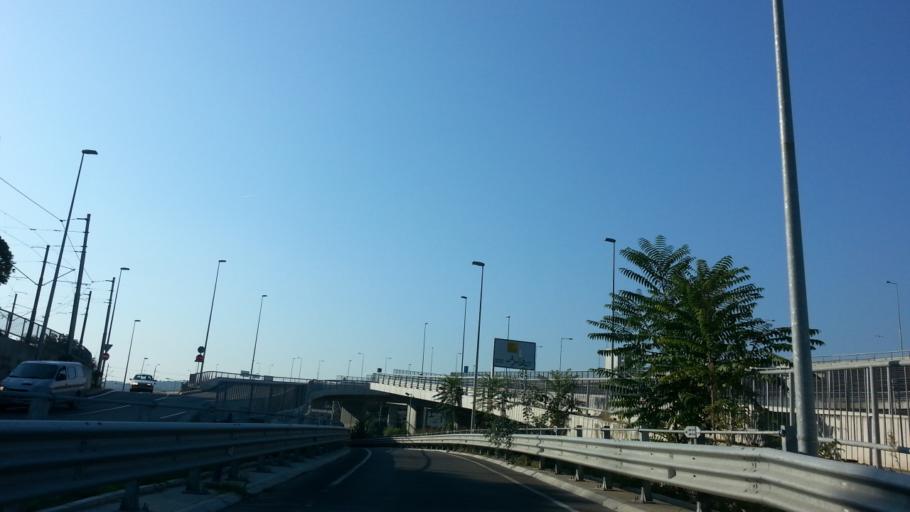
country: RS
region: Central Serbia
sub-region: Belgrade
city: Cukarica
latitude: 44.7923
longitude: 20.4281
